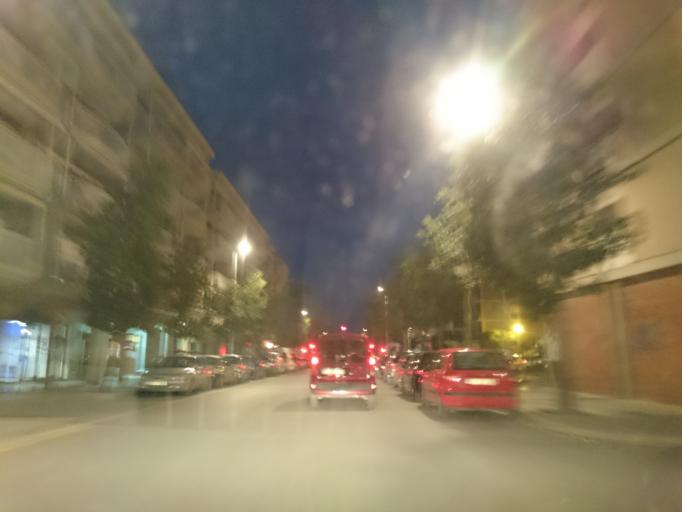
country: ES
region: Catalonia
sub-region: Provincia de Barcelona
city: Vilanova i la Geltru
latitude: 41.2214
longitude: 1.7148
